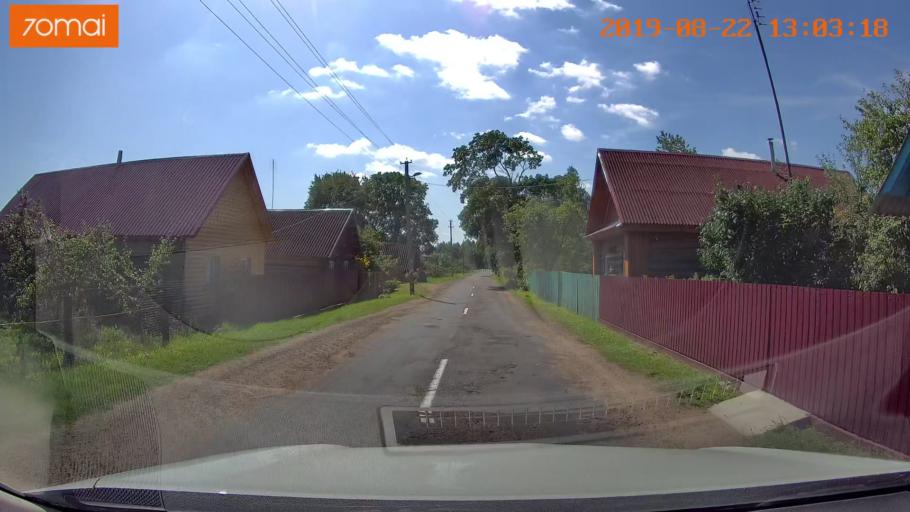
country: BY
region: Minsk
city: Prawdzinski
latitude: 53.3814
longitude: 27.8219
